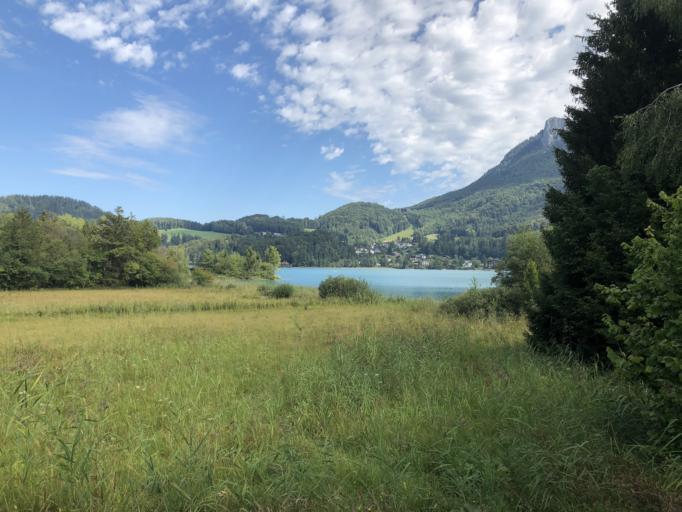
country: AT
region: Salzburg
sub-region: Politischer Bezirk Salzburg-Umgebung
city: Fuschl am See
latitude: 47.7922
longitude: 13.2924
